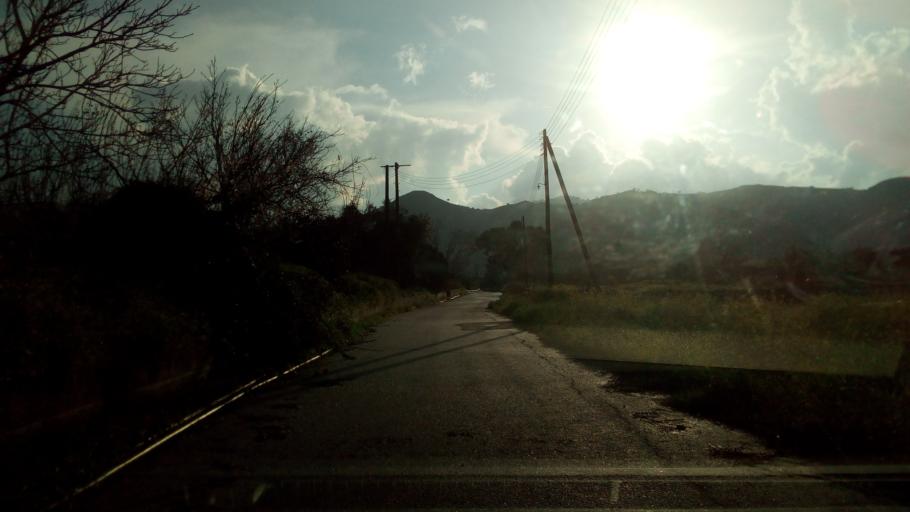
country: CY
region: Lefkosia
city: Kato Pyrgos
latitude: 35.1759
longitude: 32.6765
